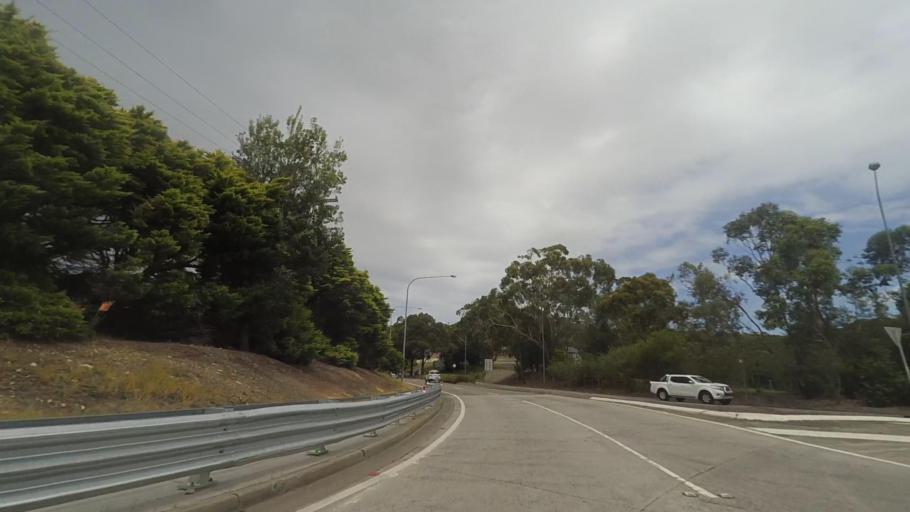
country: AU
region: New South Wales
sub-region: Wyong Shire
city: Berkeley Vale
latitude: -33.3514
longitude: 151.4335
